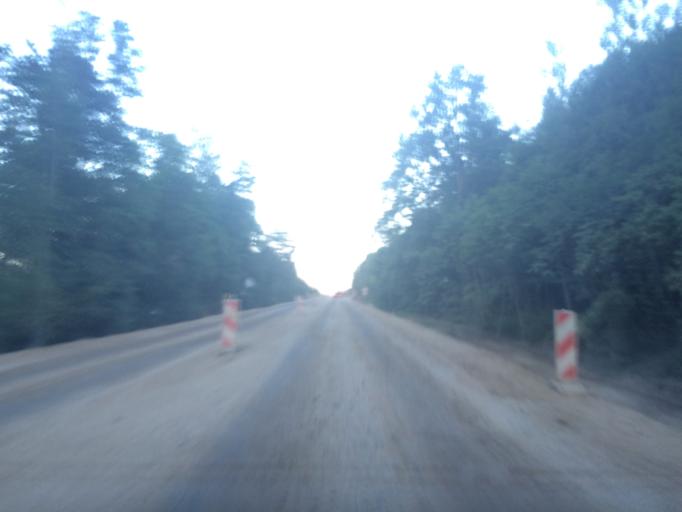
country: LT
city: Zarasai
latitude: 55.7560
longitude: 26.3257
